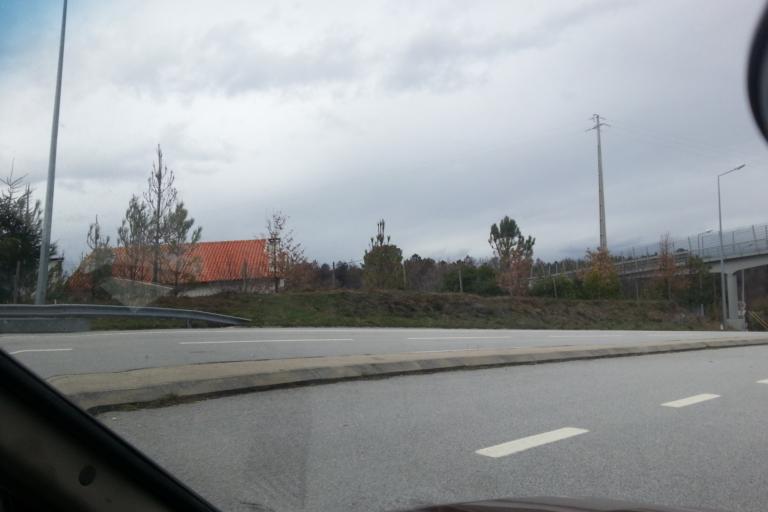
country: PT
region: Guarda
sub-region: Manteigas
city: Manteigas
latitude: 40.4753
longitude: -7.6003
